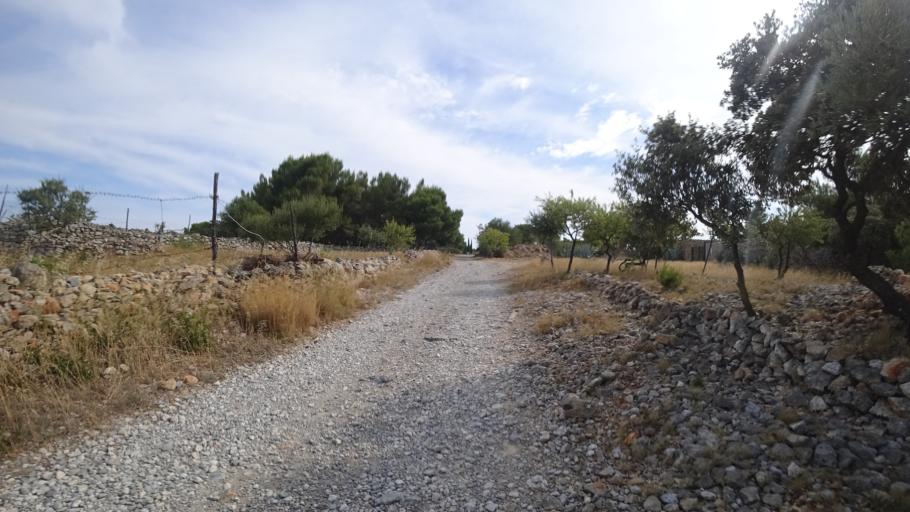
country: FR
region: Languedoc-Roussillon
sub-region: Departement de l'Aude
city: Leucate
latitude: 42.8972
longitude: 3.0341
